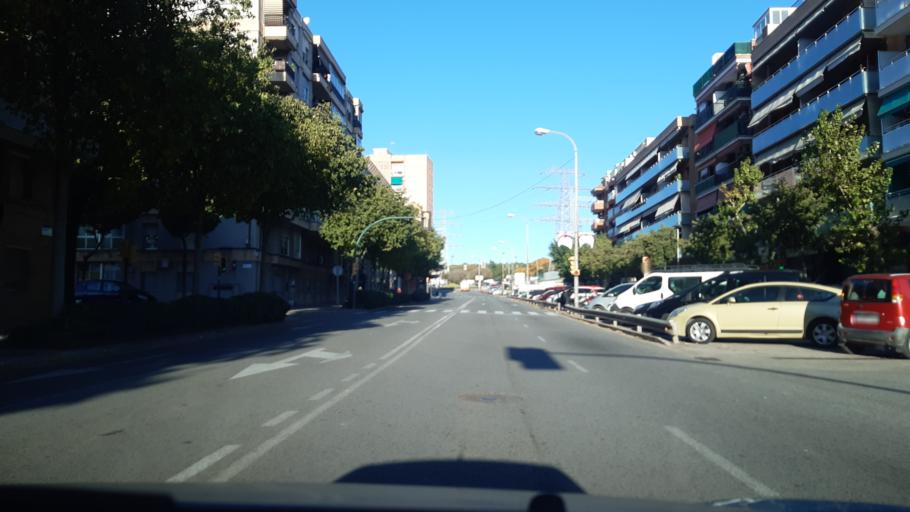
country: ES
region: Catalonia
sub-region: Provincia de Barcelona
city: Sant Boi de Llobregat
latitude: 41.3339
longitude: 2.0417
